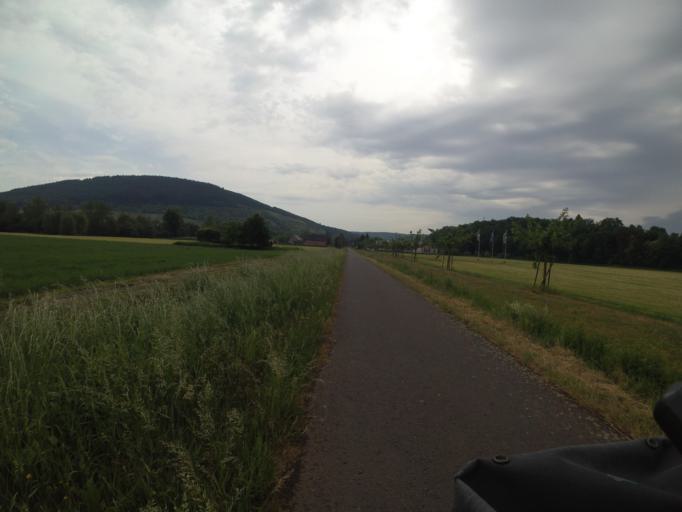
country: DE
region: Rheinland-Pfalz
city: Platten
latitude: 49.9539
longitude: 6.9476
